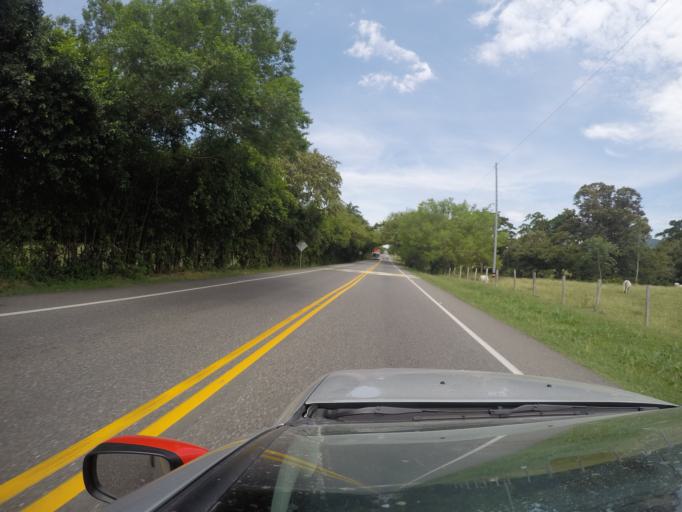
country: CO
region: Tolima
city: Honda
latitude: 5.2958
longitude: -74.7454
